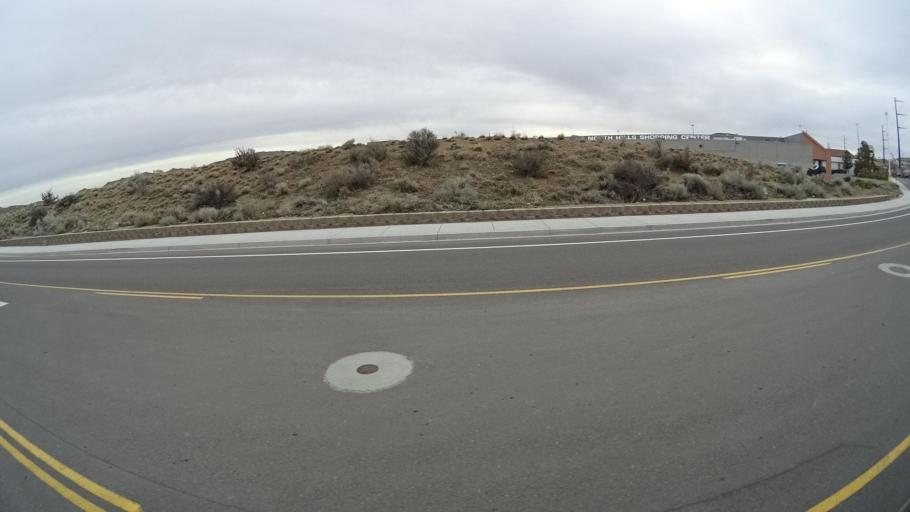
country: US
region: Nevada
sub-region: Washoe County
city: Golden Valley
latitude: 39.6055
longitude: -119.8422
